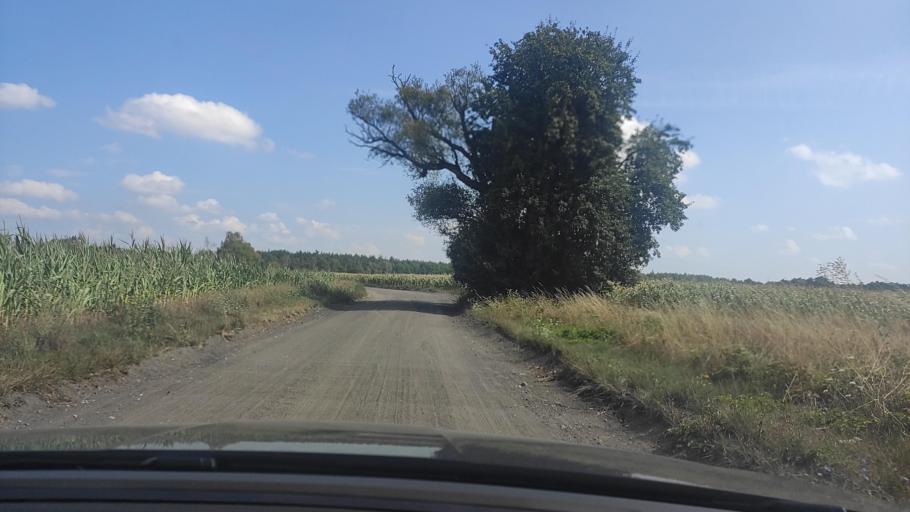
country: PL
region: Greater Poland Voivodeship
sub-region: Powiat poznanski
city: Pobiedziska
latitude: 52.4893
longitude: 17.1977
